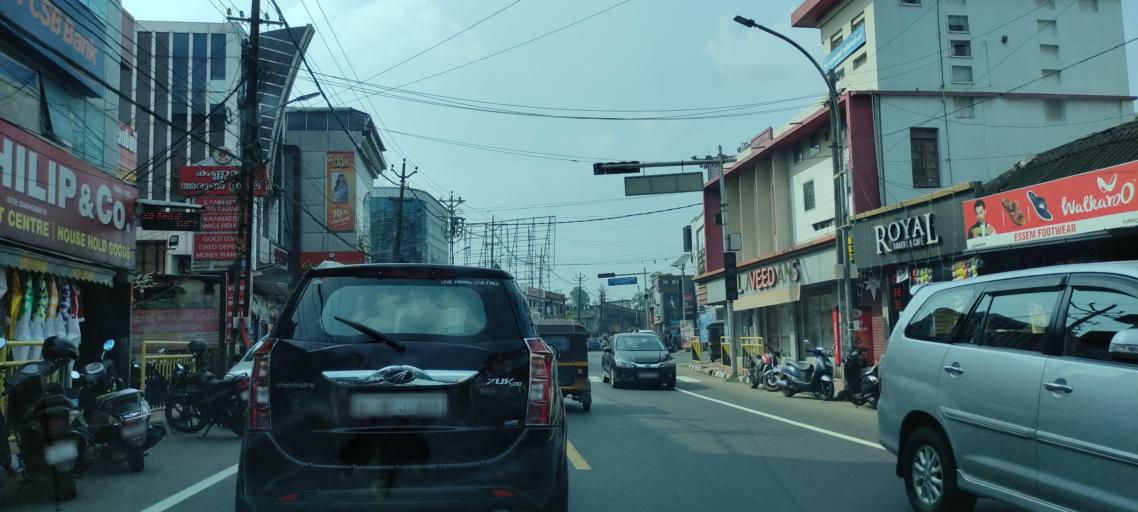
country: IN
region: Kerala
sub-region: Alappuzha
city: Chengannur
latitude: 9.3180
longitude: 76.6144
